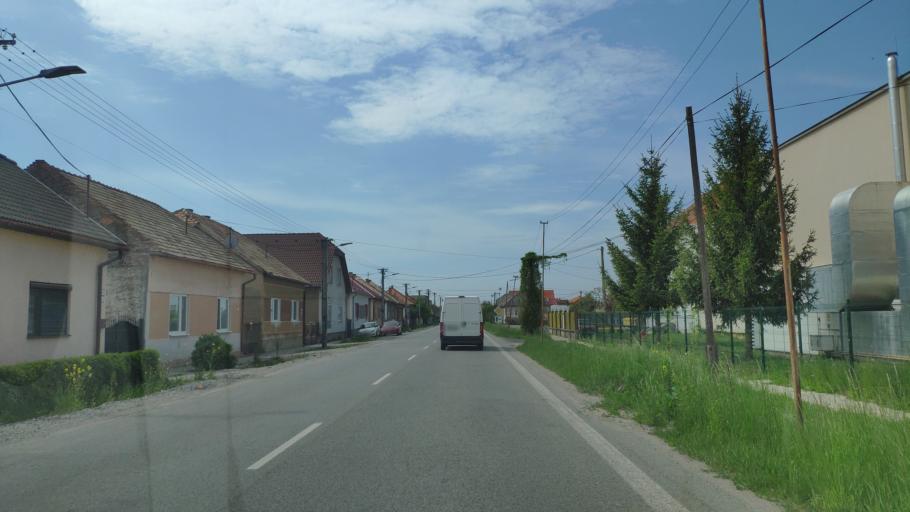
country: HU
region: Borsod-Abauj-Zemplen
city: Putnok
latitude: 48.4283
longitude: 20.3316
